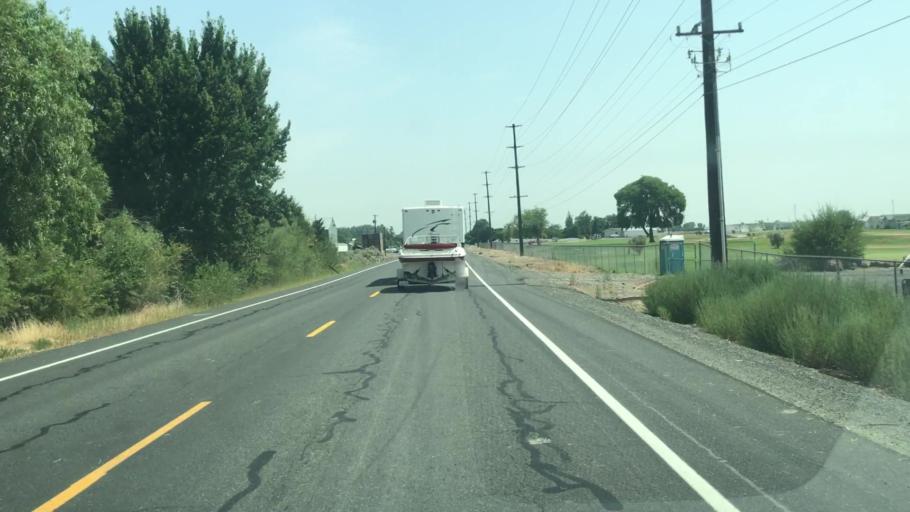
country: US
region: Washington
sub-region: Grant County
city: Quincy
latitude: 47.1613
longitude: -119.8734
